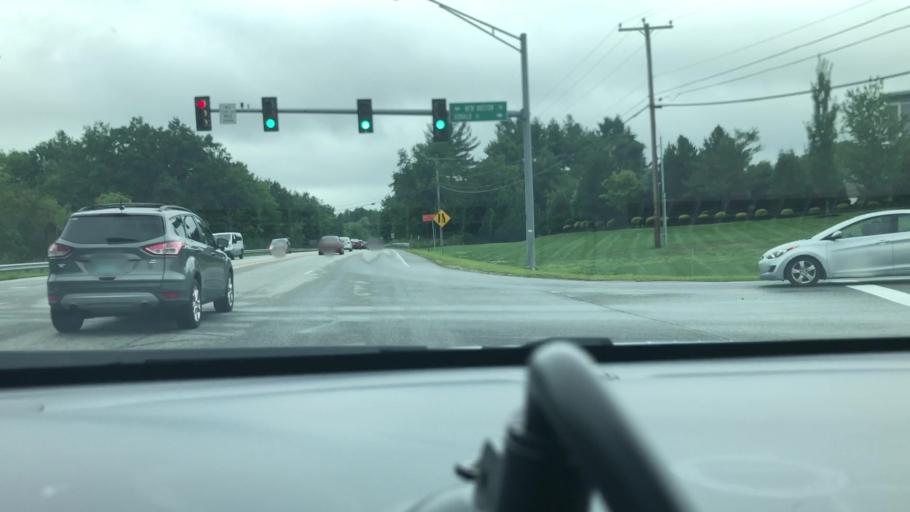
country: US
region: New Hampshire
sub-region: Hillsborough County
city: Bedford
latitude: 42.9689
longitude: -71.5086
